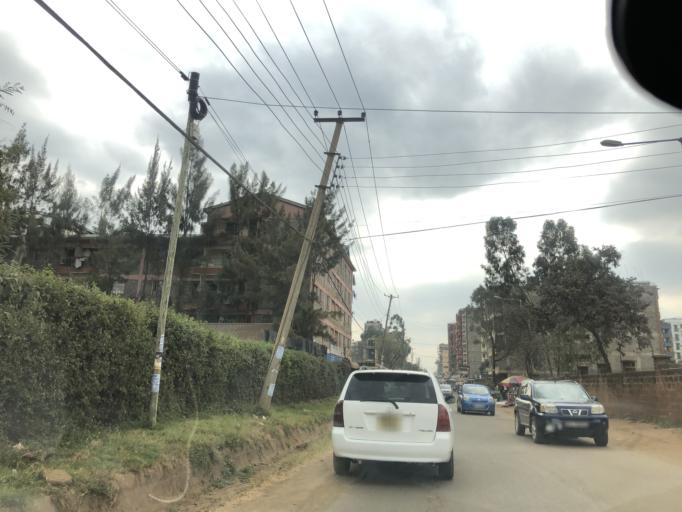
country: KE
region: Kiambu
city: Kiambu
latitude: -1.2114
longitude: 36.8881
